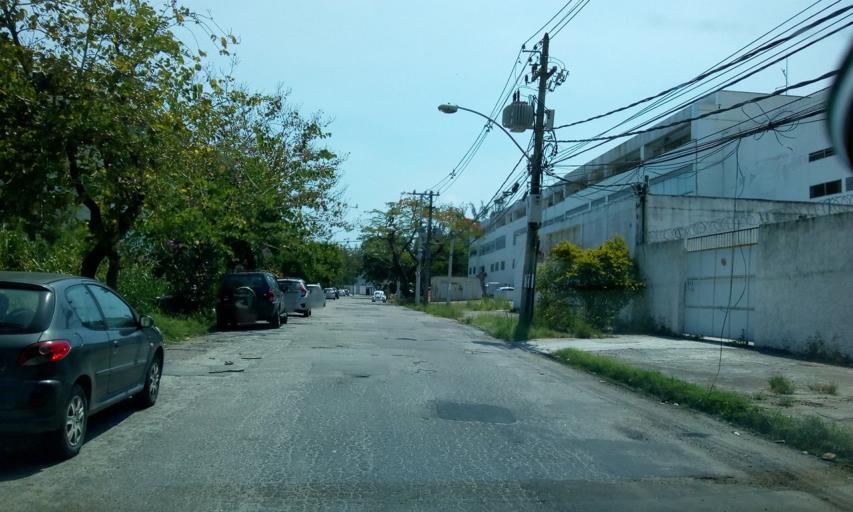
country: BR
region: Rio de Janeiro
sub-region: Nilopolis
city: Nilopolis
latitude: -23.0176
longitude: -43.4754
